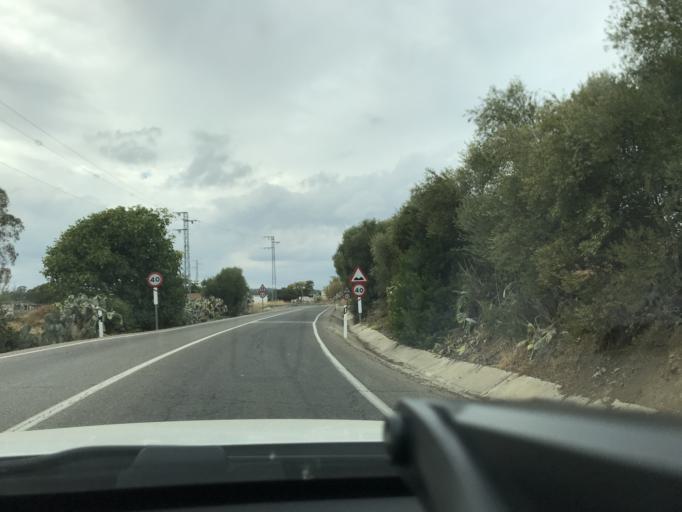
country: ES
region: Andalusia
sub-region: Provincia de Sevilla
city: Villanueva del Rio y Minas
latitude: 37.6356
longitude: -5.7296
